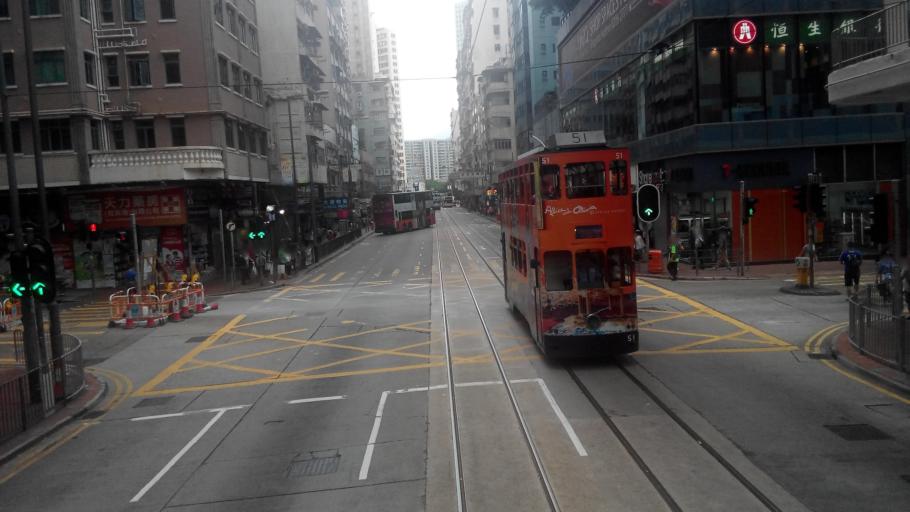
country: HK
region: Wanchai
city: Wan Chai
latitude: 22.2781
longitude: 114.2266
